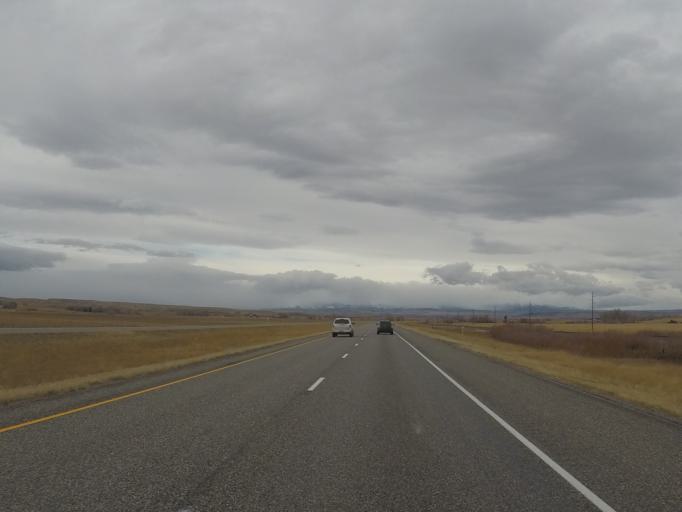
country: US
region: Montana
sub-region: Sweet Grass County
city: Big Timber
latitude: 45.7962
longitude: -109.8389
